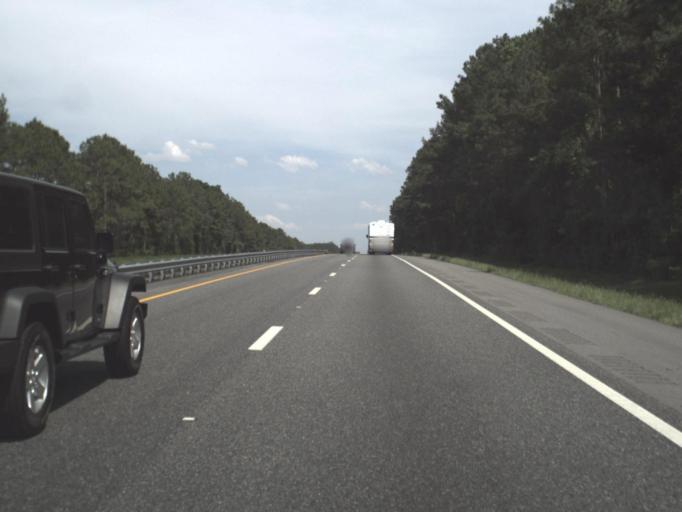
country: US
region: Florida
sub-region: Suwannee County
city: Wellborn
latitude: 30.2617
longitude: -82.7343
